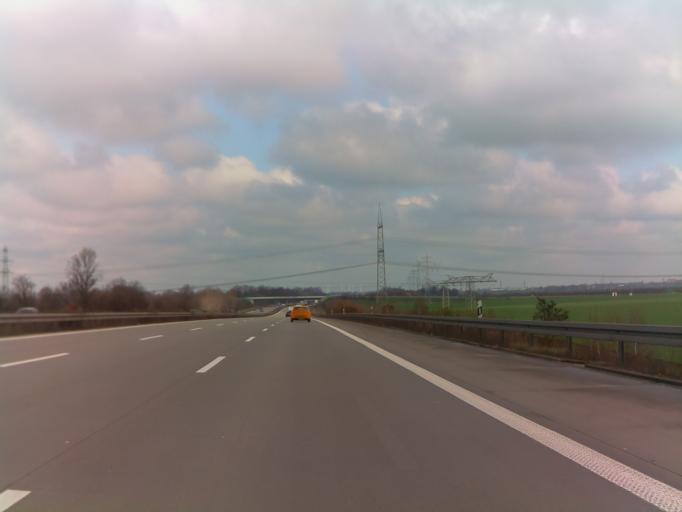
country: DE
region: Saxony
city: Wiedemar
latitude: 51.5074
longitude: 12.1998
